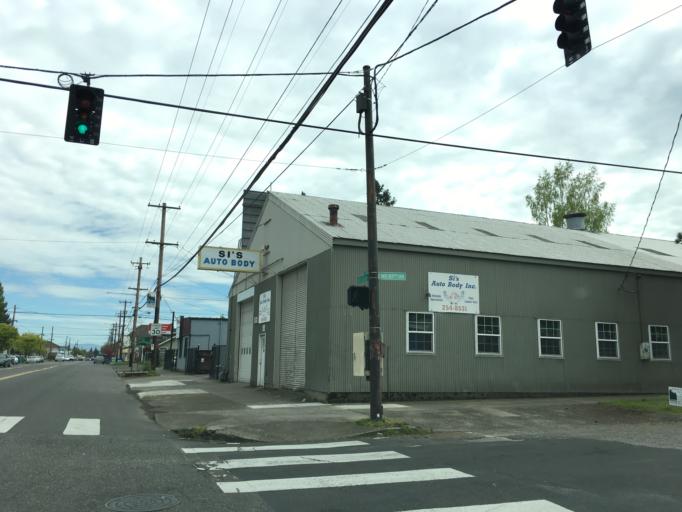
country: US
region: Oregon
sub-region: Multnomah County
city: Lents
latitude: 45.5265
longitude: -122.5946
